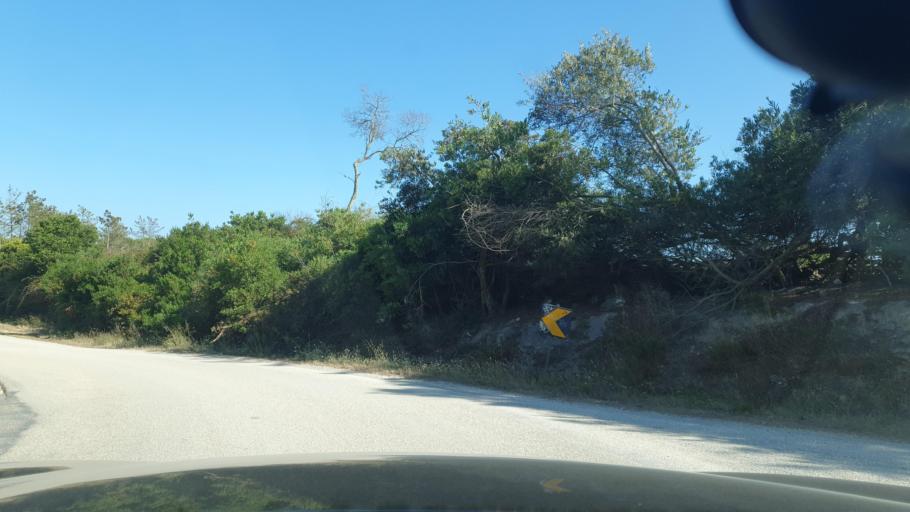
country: PT
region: Faro
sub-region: Aljezur
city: Aljezur
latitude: 37.4360
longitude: -8.7957
